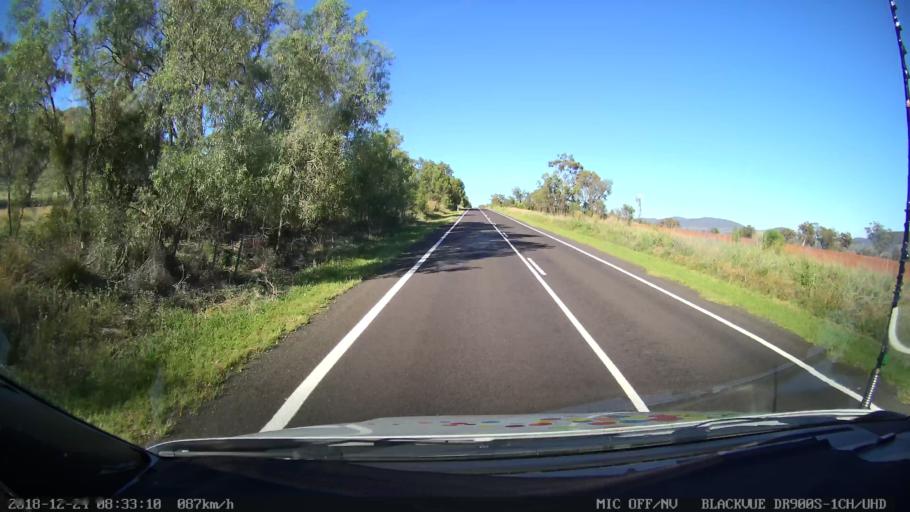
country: AU
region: New South Wales
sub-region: Tamworth Municipality
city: Phillip
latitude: -31.2847
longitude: 150.6880
